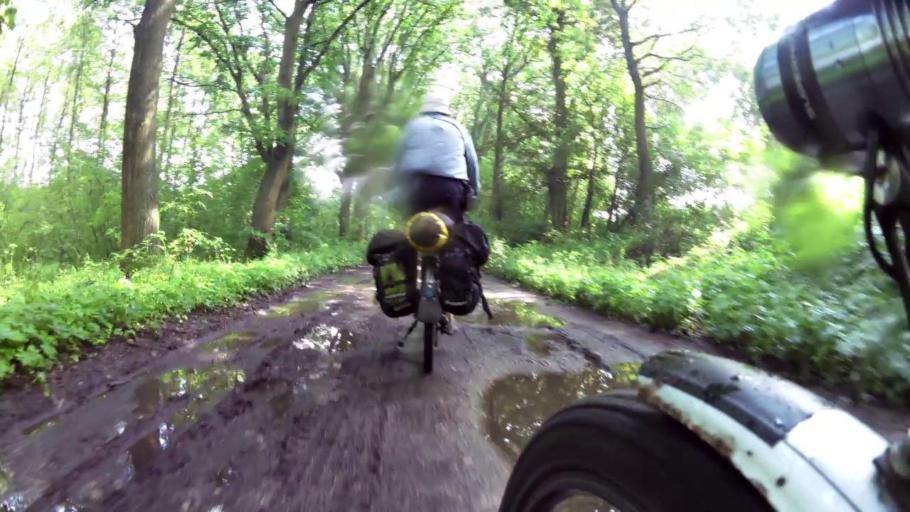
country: PL
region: West Pomeranian Voivodeship
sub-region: Powiat lobeski
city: Lobez
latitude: 53.7354
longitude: 15.6690
